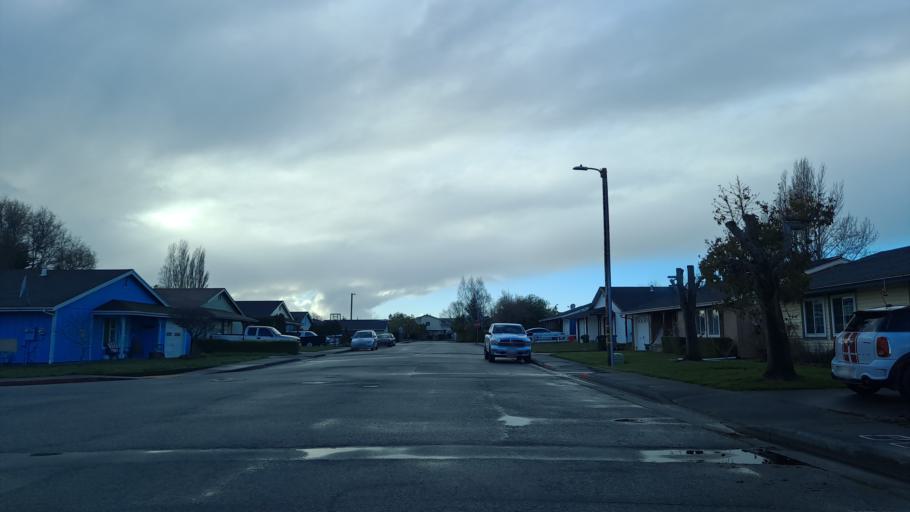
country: US
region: California
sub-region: Humboldt County
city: Fortuna
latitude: 40.5843
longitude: -124.1418
